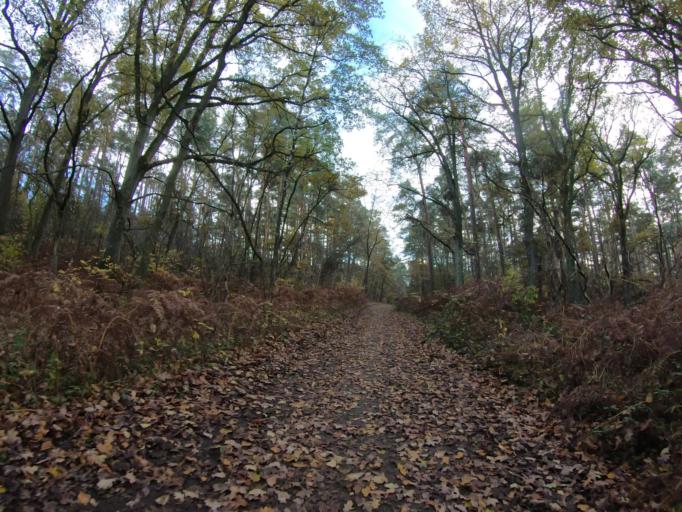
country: DE
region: Lower Saxony
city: Gifhorn
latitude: 52.4721
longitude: 10.5204
